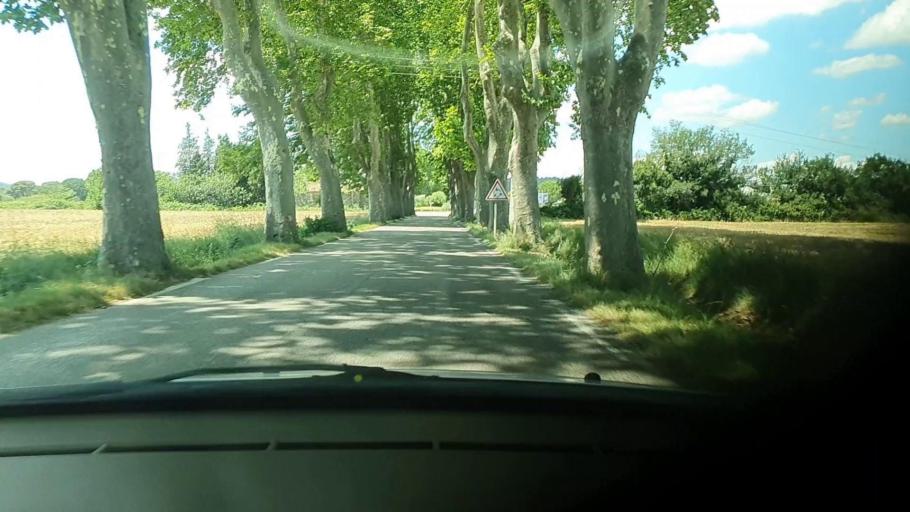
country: FR
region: Languedoc-Roussillon
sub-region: Departement du Gard
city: Montaren-et-Saint-Mediers
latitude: 44.0238
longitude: 4.3912
